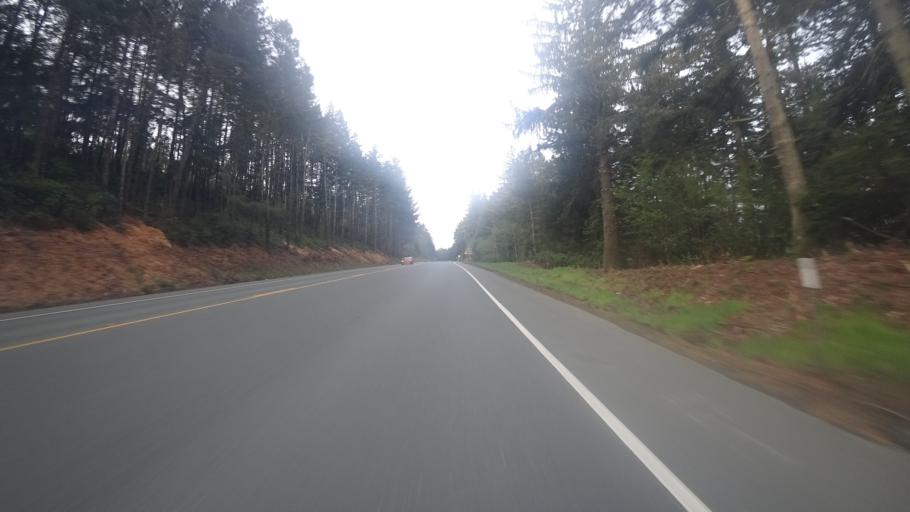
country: US
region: Oregon
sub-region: Coos County
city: Lakeside
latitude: 43.5694
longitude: -124.2002
